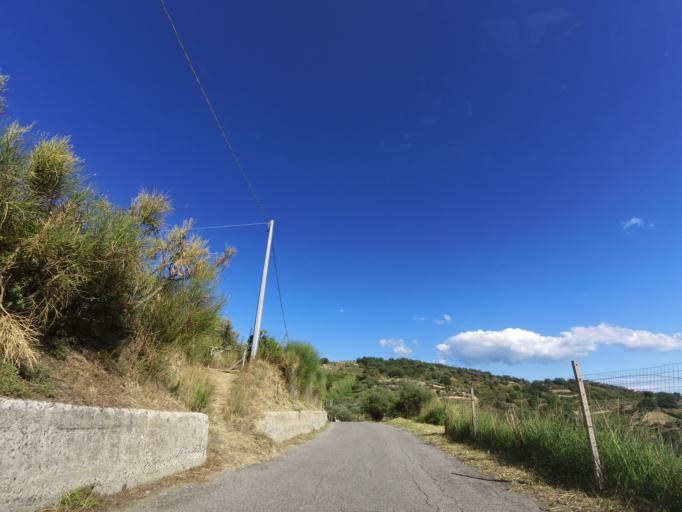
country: IT
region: Calabria
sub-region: Provincia di Reggio Calabria
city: Pazzano
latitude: 38.4537
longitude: 16.4487
